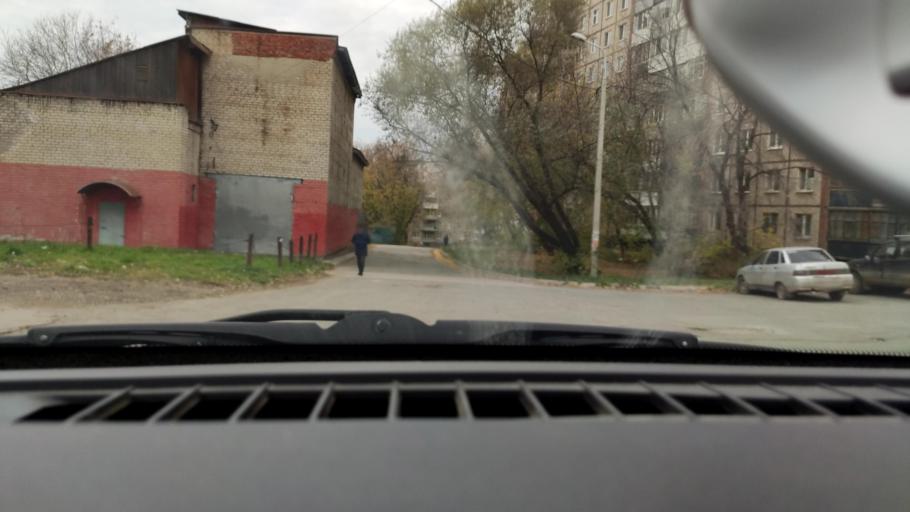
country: RU
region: Perm
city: Perm
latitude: 57.9725
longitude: 56.2310
